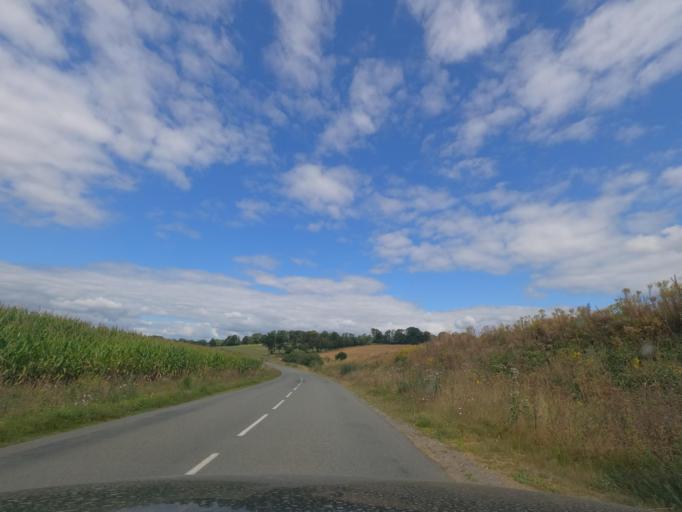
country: FR
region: Pays de la Loire
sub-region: Departement de la Mayenne
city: Landivy
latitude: 48.4653
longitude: -1.0477
